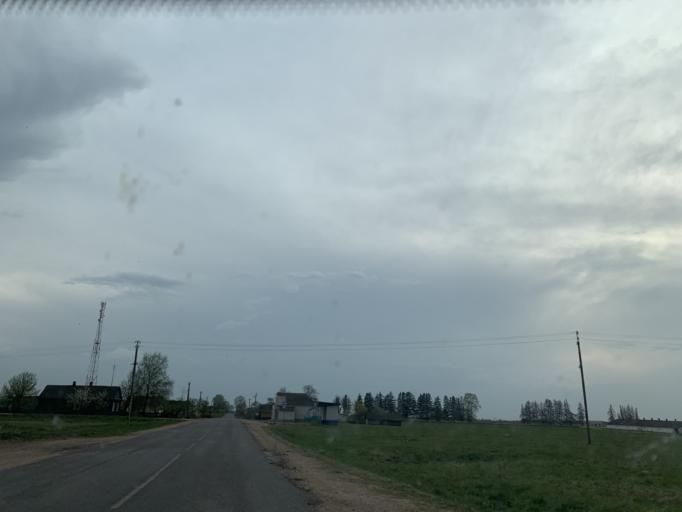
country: BY
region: Minsk
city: Kapyl'
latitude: 53.2801
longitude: 26.9766
